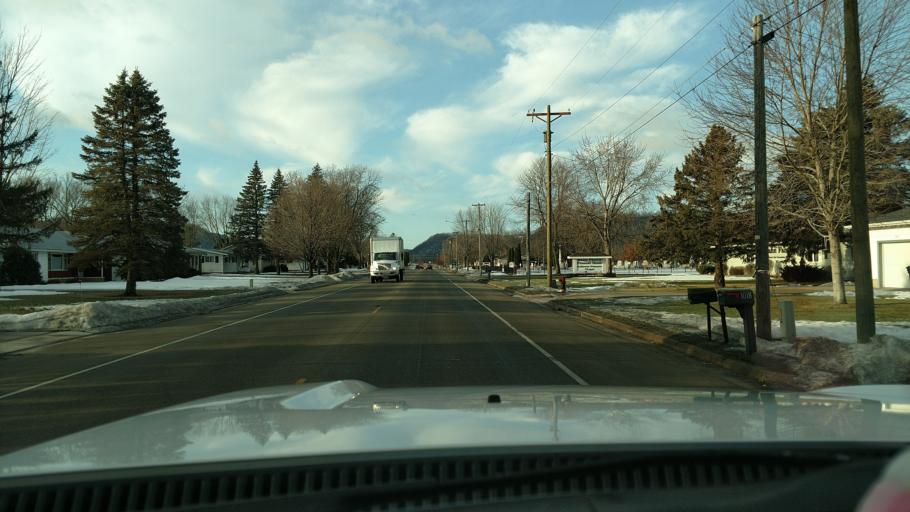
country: US
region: Minnesota
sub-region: Wabasha County
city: Lake City
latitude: 44.4409
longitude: -92.2772
